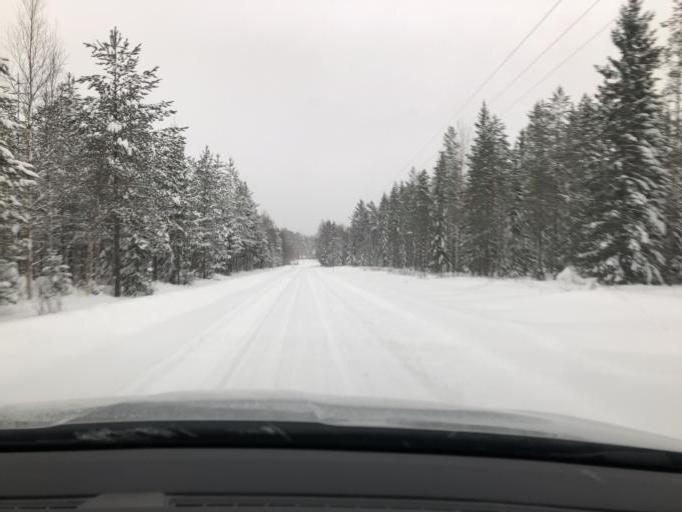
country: SE
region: Vaesterbotten
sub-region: Umea Kommun
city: Saevar
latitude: 63.9454
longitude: 20.7033
